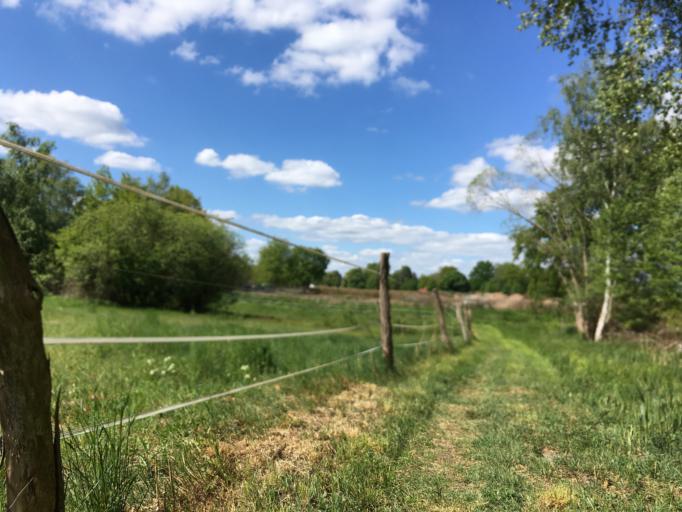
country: DE
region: Berlin
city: Blankenfelde
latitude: 52.6549
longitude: 13.3795
